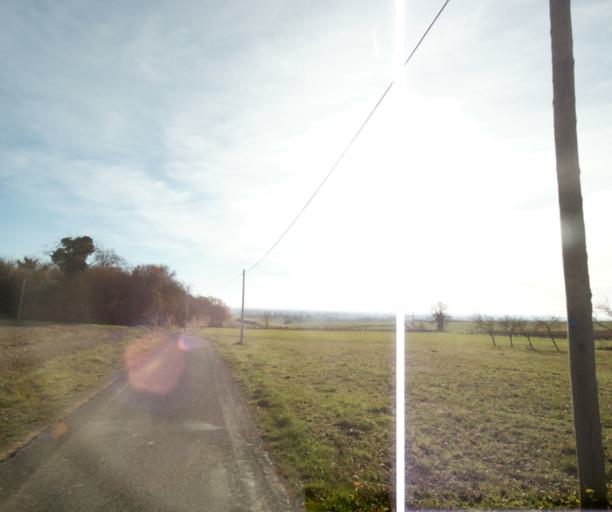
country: FR
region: Poitou-Charentes
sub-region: Departement de la Charente-Maritime
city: Chaniers
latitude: 45.7287
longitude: -0.5443
